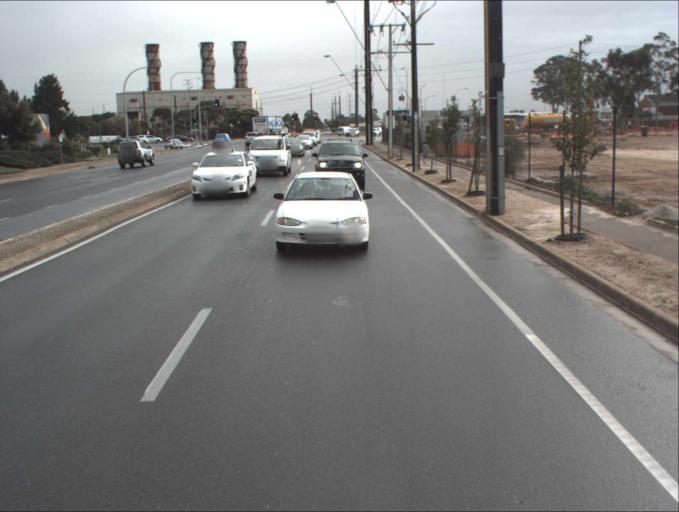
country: AU
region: South Australia
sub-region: Port Adelaide Enfield
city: Blair Athol
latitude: -34.8505
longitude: 138.5825
